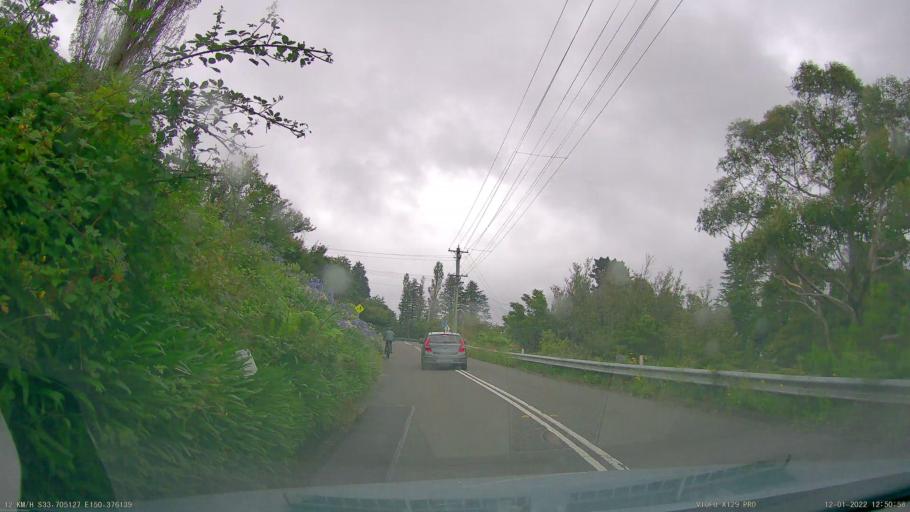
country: AU
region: New South Wales
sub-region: Blue Mountains Municipality
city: Leura
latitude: -33.7051
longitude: 150.3761
